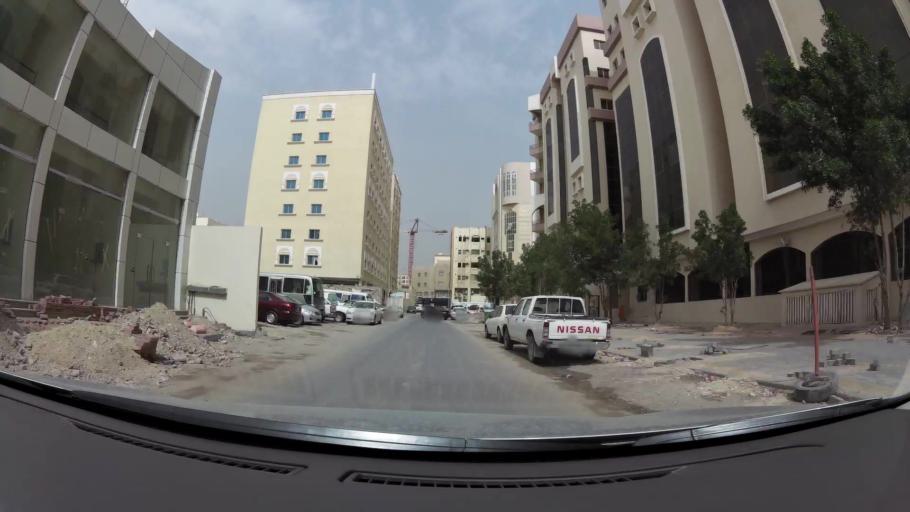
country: QA
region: Baladiyat ad Dawhah
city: Doha
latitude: 25.2699
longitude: 51.5444
